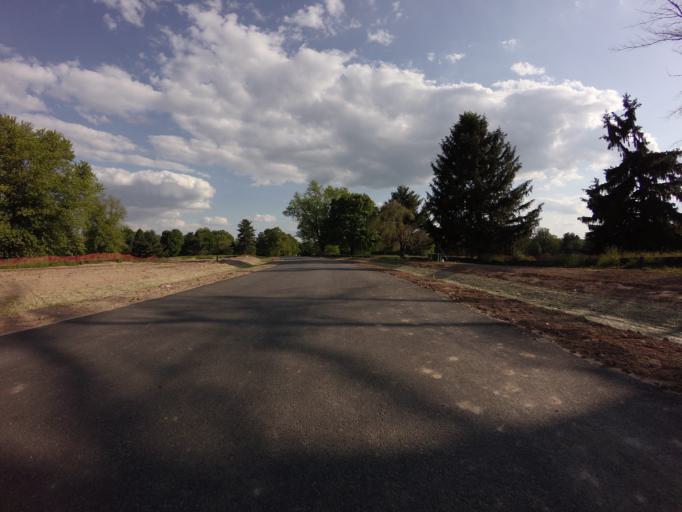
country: US
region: Maryland
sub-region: Baltimore County
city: Mays Chapel
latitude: 39.4433
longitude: -76.6908
